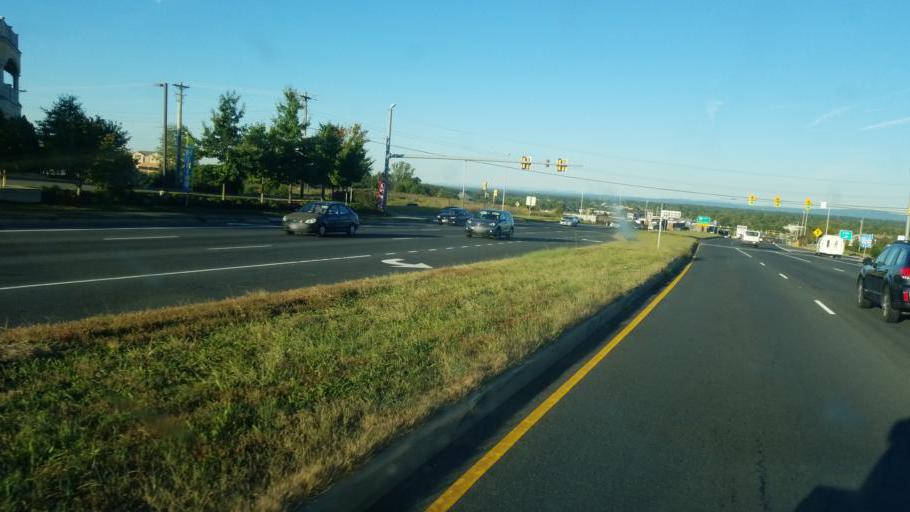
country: US
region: Virginia
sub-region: Fairfax County
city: Centreville
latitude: 38.8389
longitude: -77.4290
